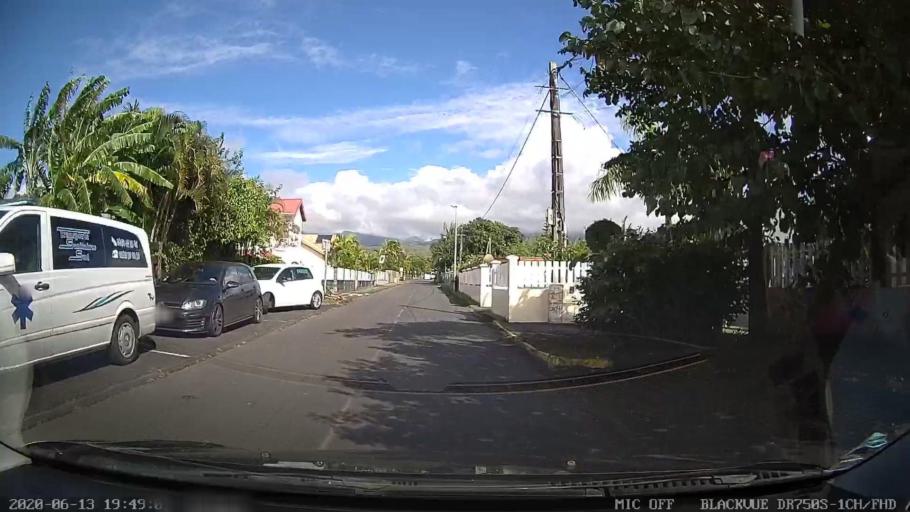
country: RE
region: Reunion
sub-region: Reunion
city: Bras-Panon
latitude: -21.0036
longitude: 55.6902
